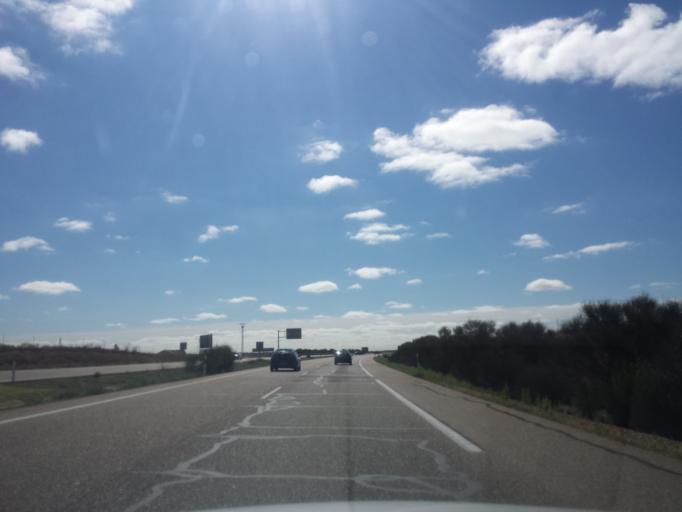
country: ES
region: Castille and Leon
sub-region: Provincia de Zamora
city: Villalpando
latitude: 41.8541
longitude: -5.4124
